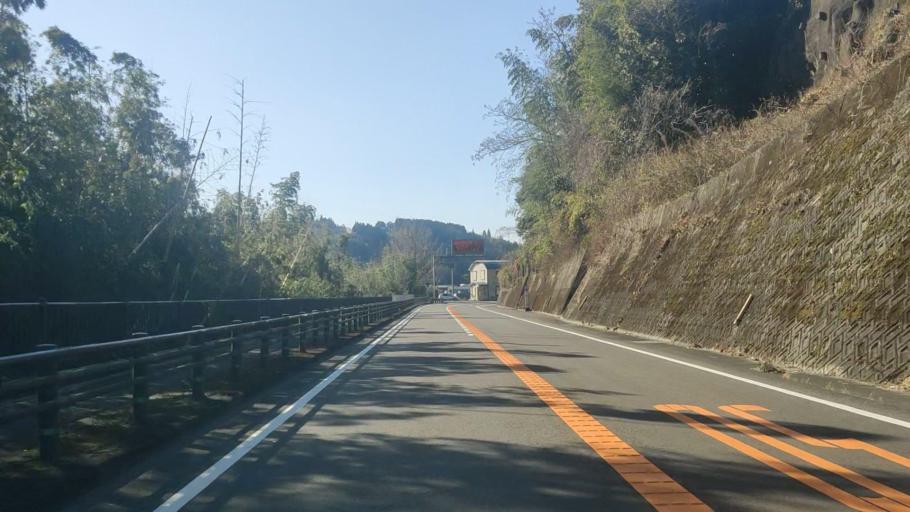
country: JP
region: Oita
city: Usuki
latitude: 33.0702
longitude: 131.6423
